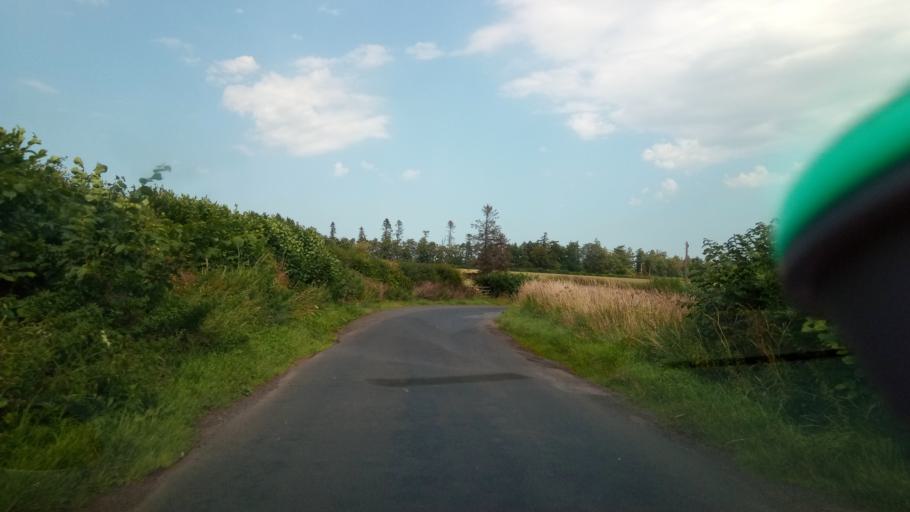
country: GB
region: Scotland
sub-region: The Scottish Borders
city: Kelso
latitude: 55.5882
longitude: -2.4708
